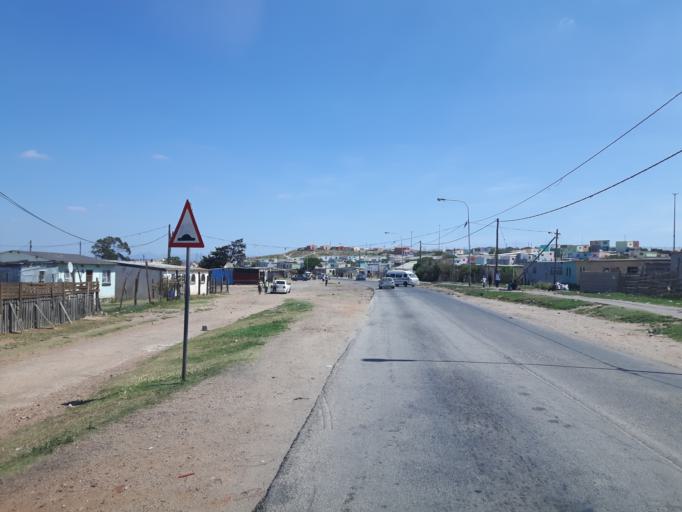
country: ZA
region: Eastern Cape
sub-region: Nelson Mandela Bay Metropolitan Municipality
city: Port Elizabeth
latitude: -33.8847
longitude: 25.5570
